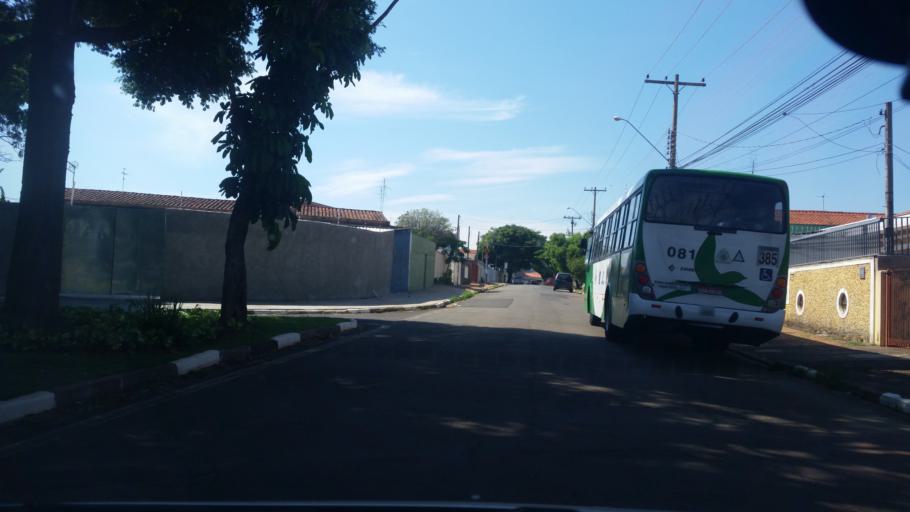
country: BR
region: Sao Paulo
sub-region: Campinas
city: Campinas
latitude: -22.8689
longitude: -47.0652
